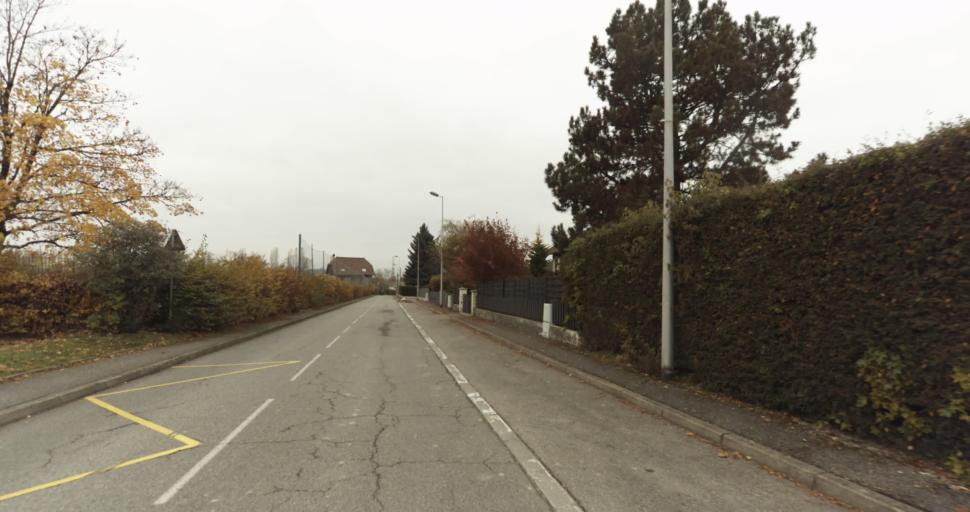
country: FR
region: Rhone-Alpes
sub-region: Departement de la Haute-Savoie
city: Seynod
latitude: 45.8872
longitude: 6.0918
